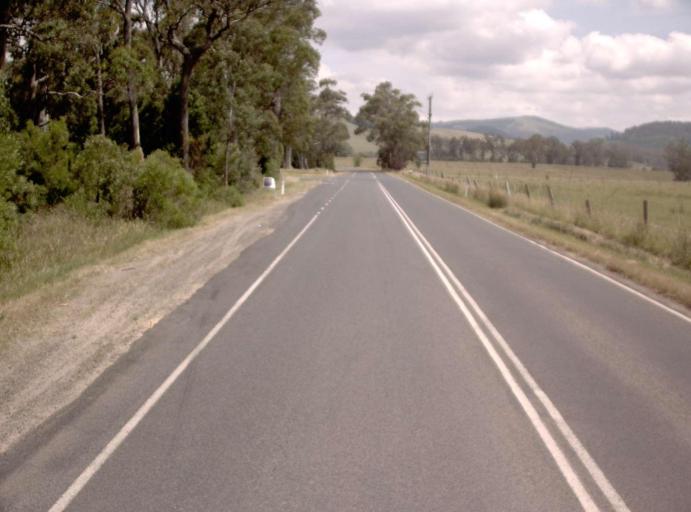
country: AU
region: Victoria
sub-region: Latrobe
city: Traralgon
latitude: -38.2959
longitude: 146.5381
